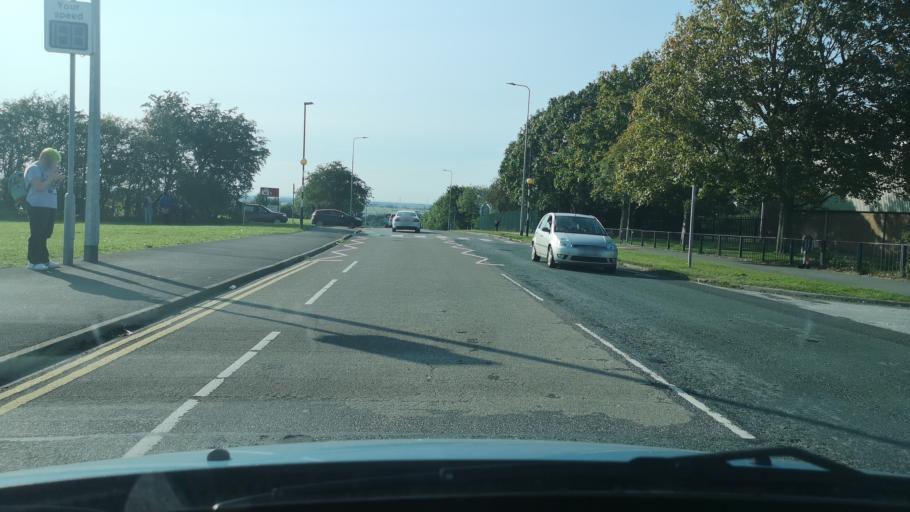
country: GB
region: England
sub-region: North Lincolnshire
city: Scunthorpe
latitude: 53.5741
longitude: -0.6680
